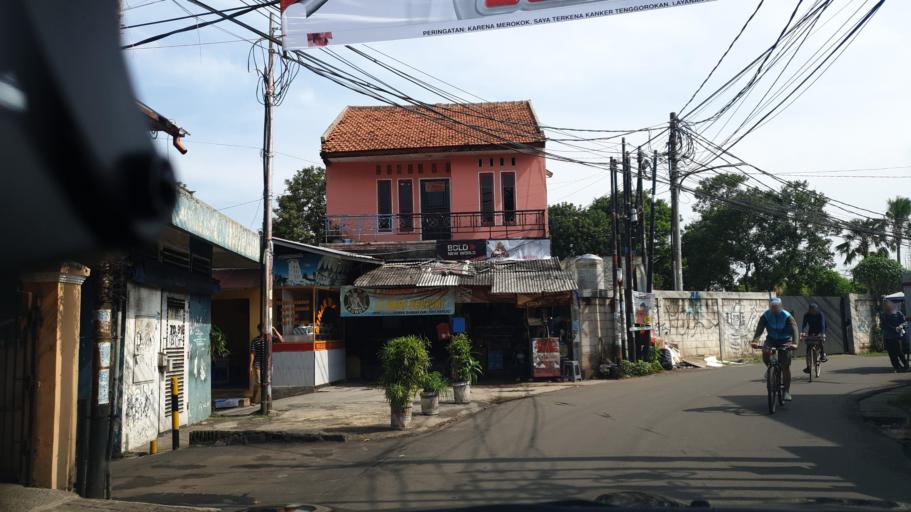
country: ID
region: West Java
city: Pamulang
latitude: -6.3033
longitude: 106.7654
